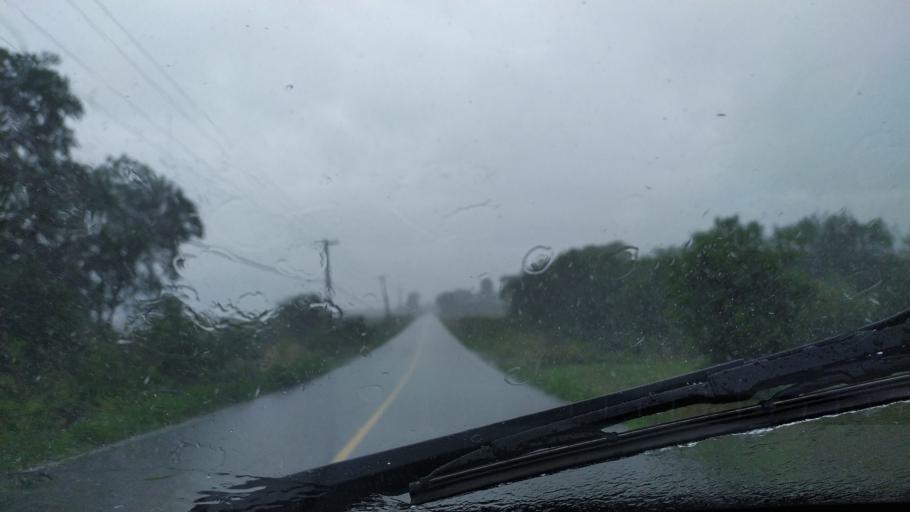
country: CA
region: Ontario
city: Prince Edward
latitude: 43.9706
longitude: -77.4164
